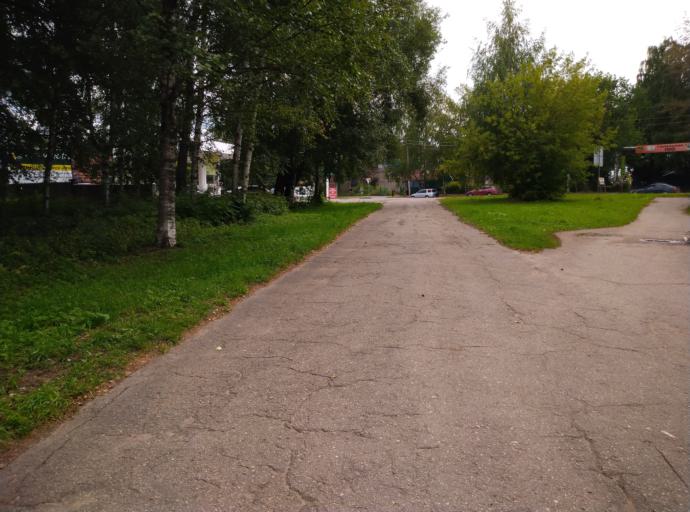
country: RU
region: Kostroma
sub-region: Kostromskoy Rayon
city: Kostroma
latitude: 57.7801
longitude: 40.9623
